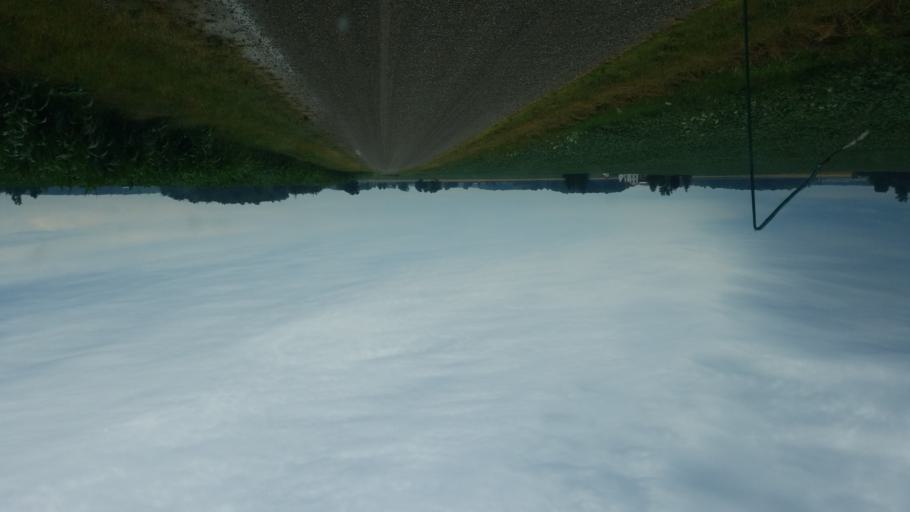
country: US
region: Indiana
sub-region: DeKalb County
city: Butler
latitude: 41.4462
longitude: -84.9098
